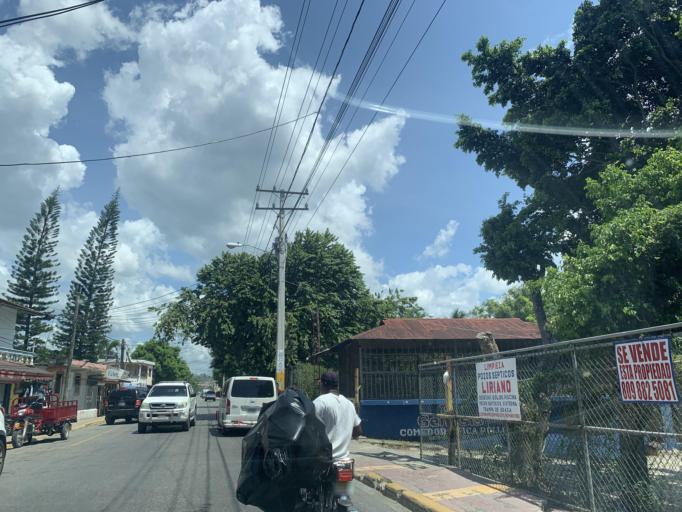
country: DO
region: Espaillat
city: Jamao al Norte
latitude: 19.6667
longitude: -70.3671
